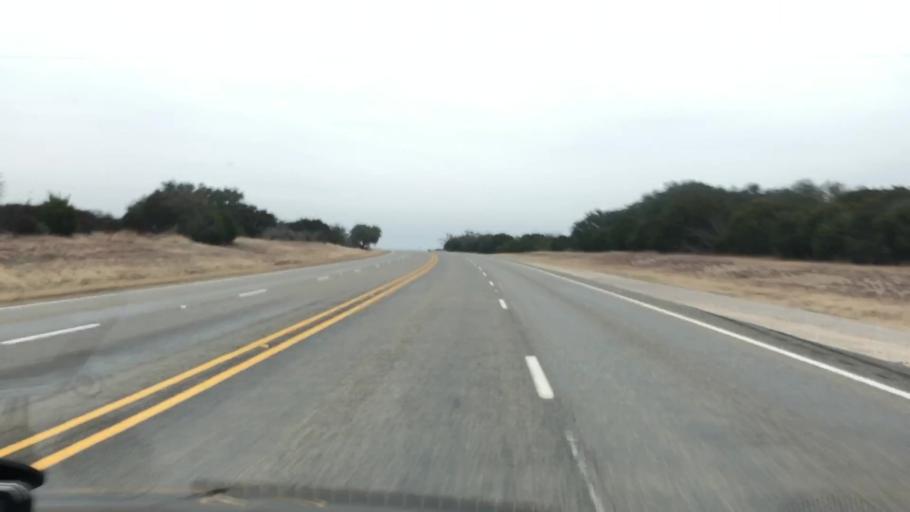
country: US
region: Texas
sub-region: Lampasas County
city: Lampasas
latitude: 31.1894
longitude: -98.1718
